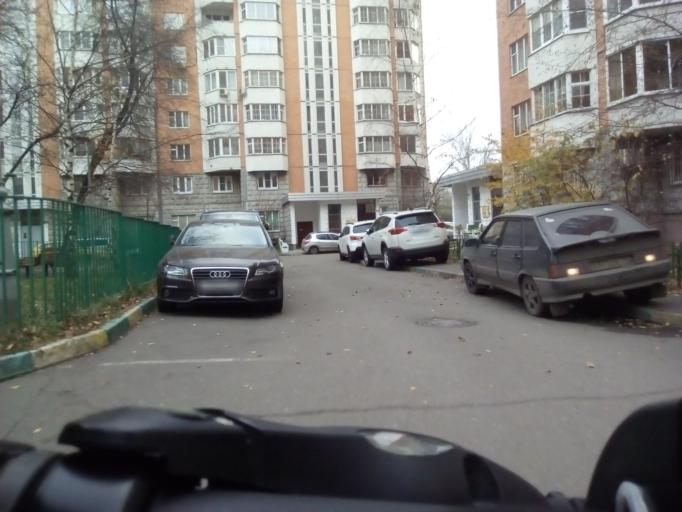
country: RU
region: Moscow
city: Lefortovo
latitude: 55.7742
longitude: 37.7097
